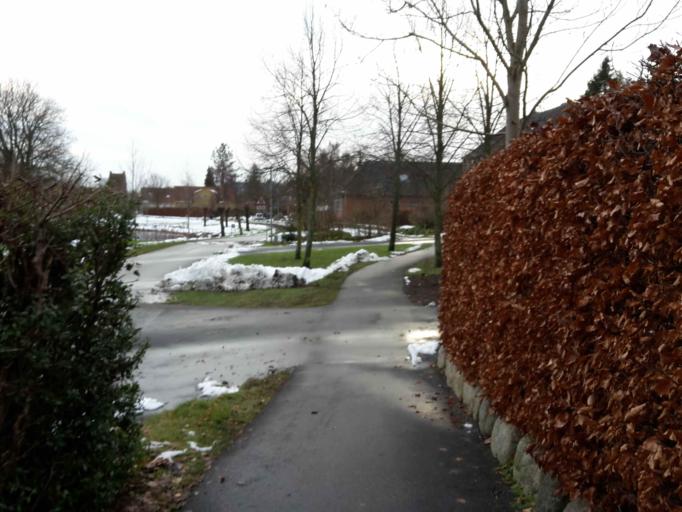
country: DK
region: Capital Region
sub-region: Allerod Kommune
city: Blovstrod
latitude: 55.8675
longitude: 12.3873
